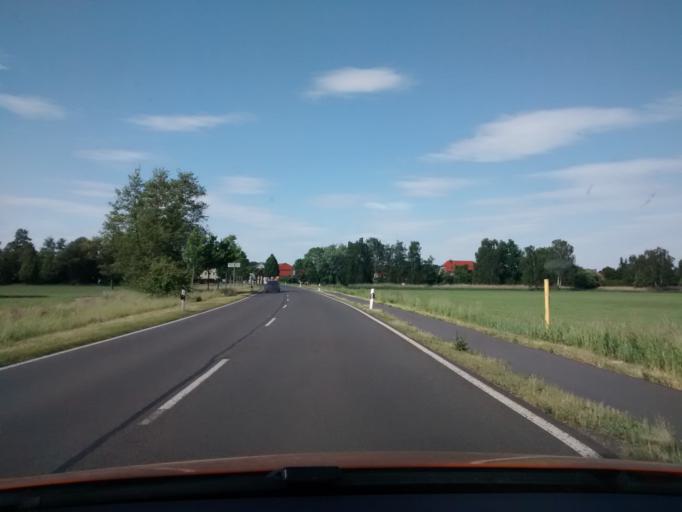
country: DE
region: Brandenburg
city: Juterbog
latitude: 52.0174
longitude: 13.1018
